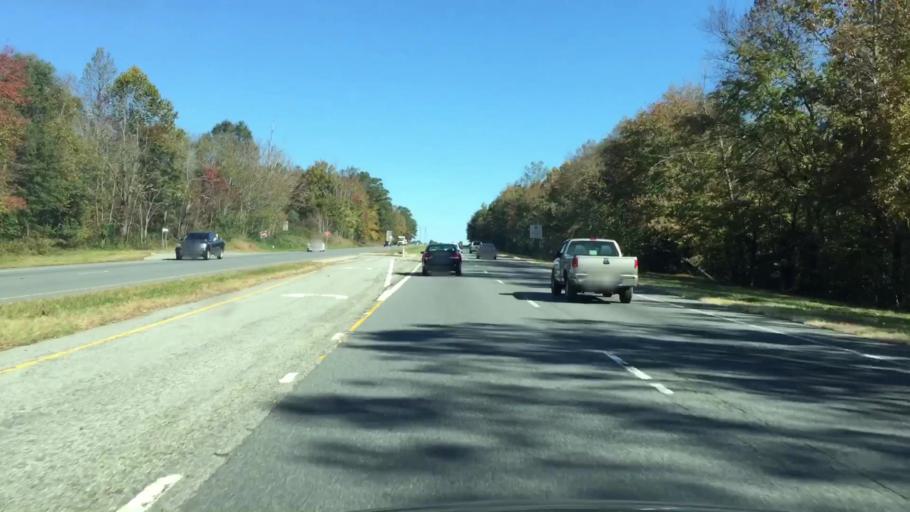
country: US
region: North Carolina
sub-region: Guilford County
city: McLeansville
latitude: 36.2052
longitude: -79.6936
